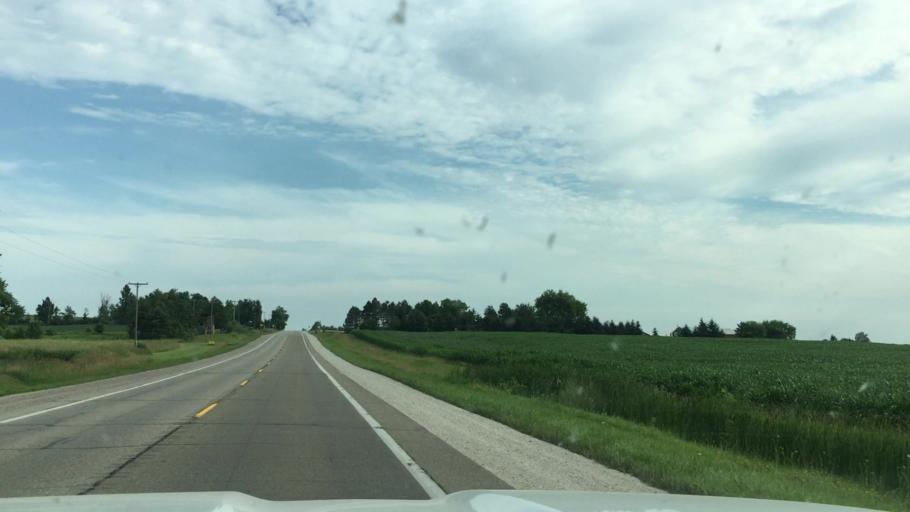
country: US
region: Michigan
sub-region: Sanilac County
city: Brown City
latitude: 43.1933
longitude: -83.0768
